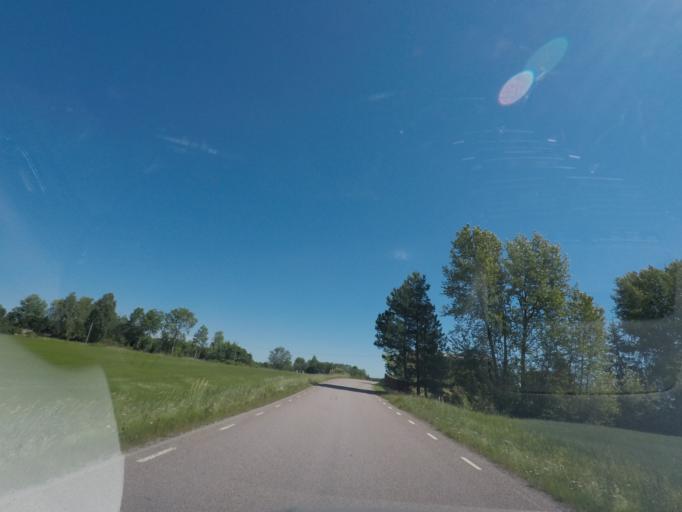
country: SE
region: Uppsala
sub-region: Enkopings Kommun
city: Irsta
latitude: 59.6810
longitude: 16.8203
